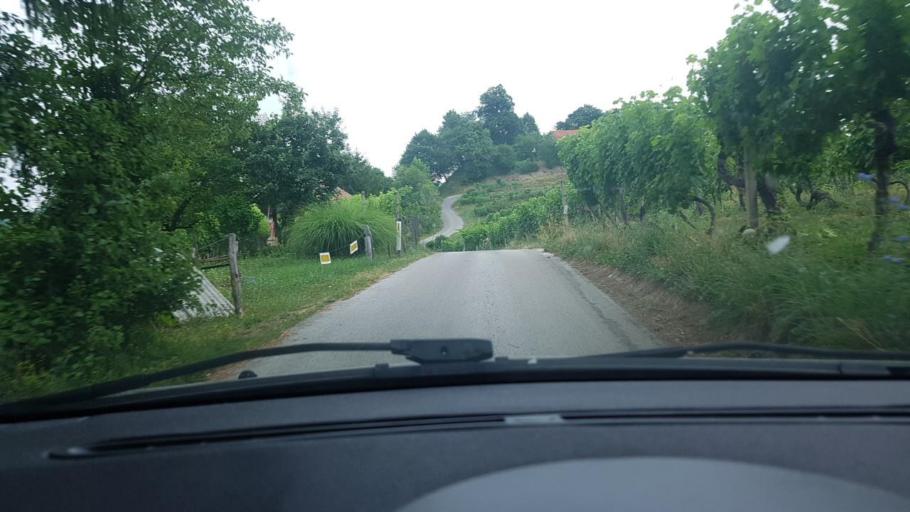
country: SI
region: Podlehnik
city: Podlehnik
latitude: 46.3326
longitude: 15.9028
